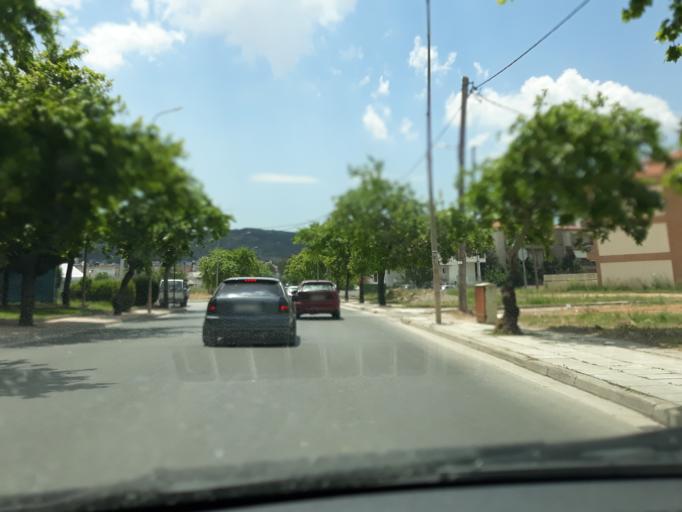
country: GR
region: Attica
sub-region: Nomarchia Dytikis Attikis
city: Ano Liosia
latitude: 38.0772
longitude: 23.7085
